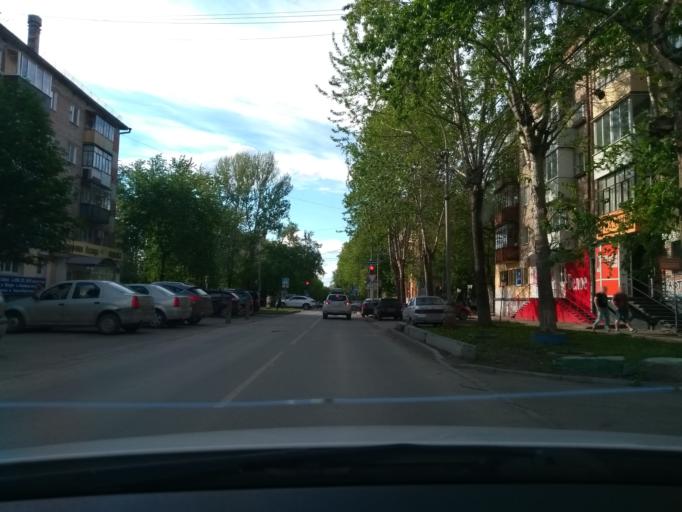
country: RU
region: Perm
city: Perm
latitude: 57.9993
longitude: 56.2557
